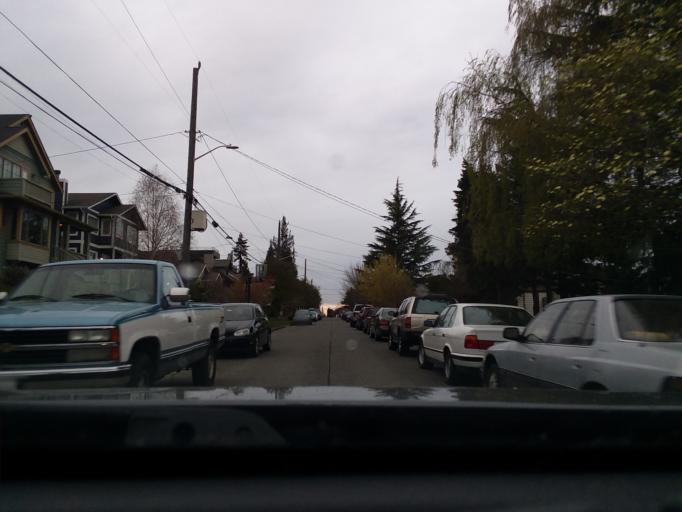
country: US
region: Washington
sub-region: King County
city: Shoreline
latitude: 47.6854
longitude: -122.3957
